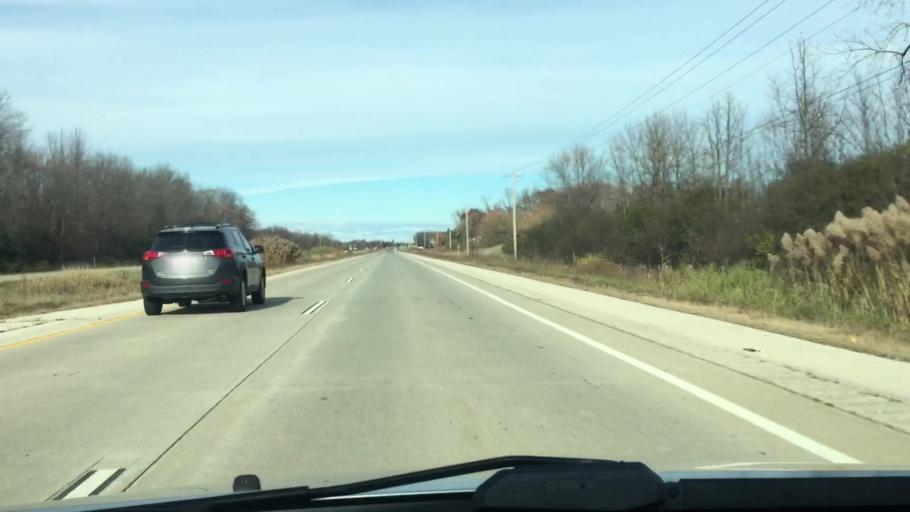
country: US
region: Wisconsin
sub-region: Brown County
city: Bellevue
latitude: 44.5615
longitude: -87.8804
